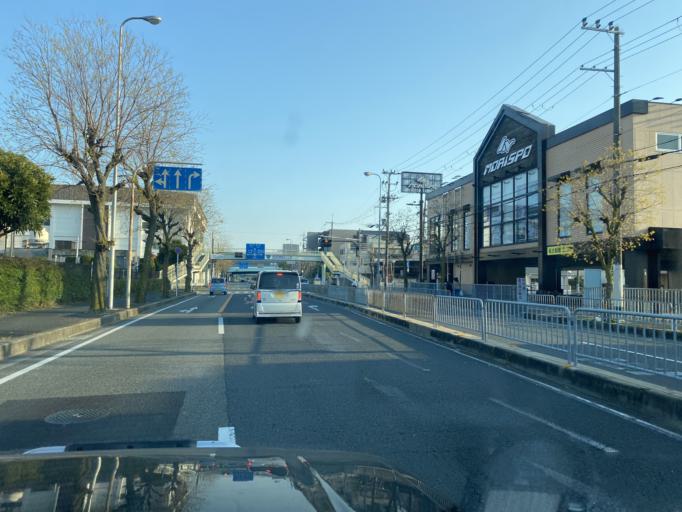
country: JP
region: Osaka
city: Ikeda
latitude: 34.8090
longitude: 135.4315
